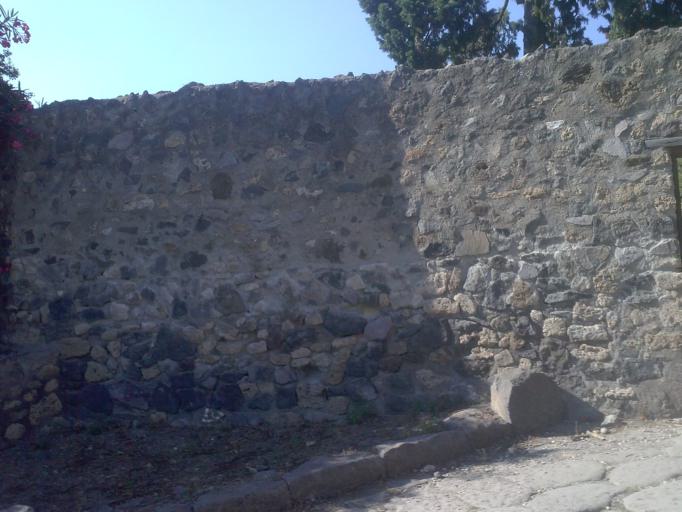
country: IT
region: Campania
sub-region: Provincia di Napoli
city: Pompei
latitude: 40.7518
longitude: 14.4809
